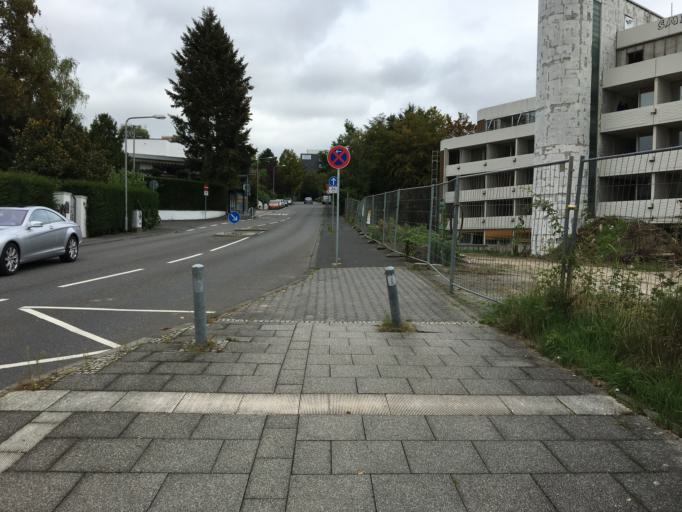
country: DE
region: Hesse
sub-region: Regierungsbezirk Darmstadt
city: Wiesbaden
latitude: 50.0904
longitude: 8.2637
